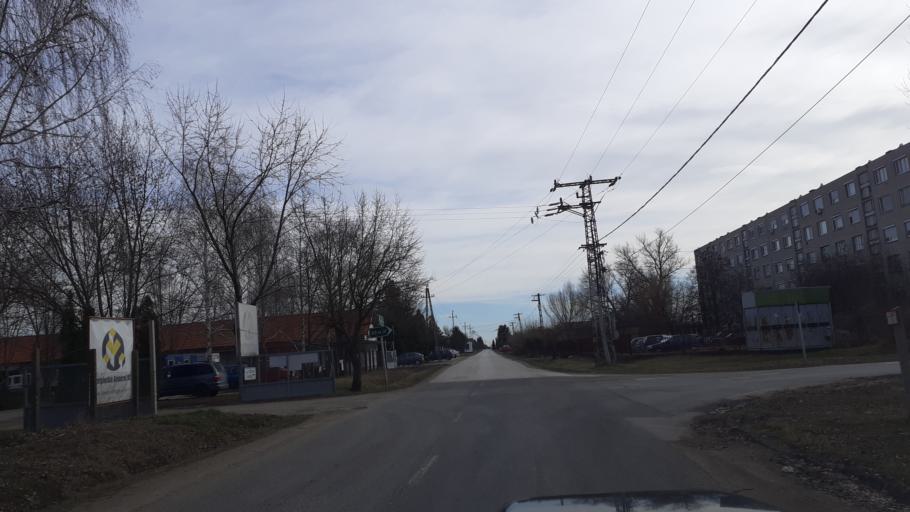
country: HU
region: Fejer
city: Sarbogard
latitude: 46.8916
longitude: 18.6268
